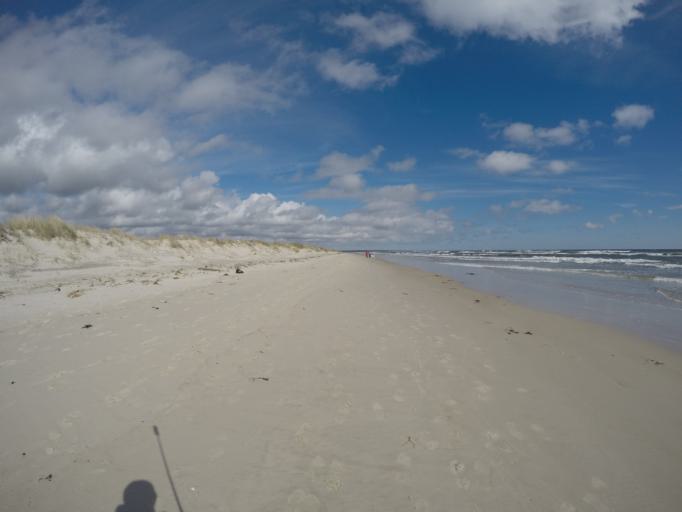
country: SE
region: Skane
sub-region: Simrishamns Kommun
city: Simrishamn
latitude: 55.3980
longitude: 14.2131
